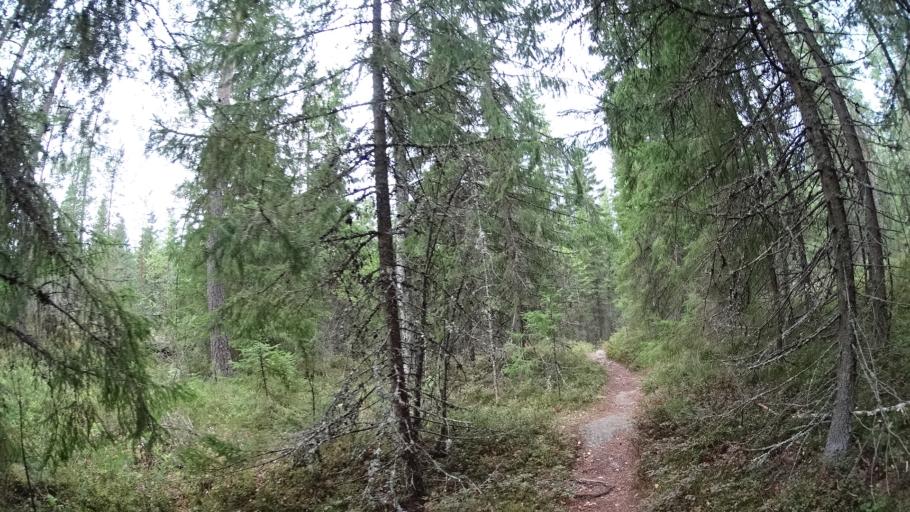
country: FI
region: Uusimaa
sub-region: Helsinki
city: Espoo
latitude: 60.3088
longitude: 24.5792
